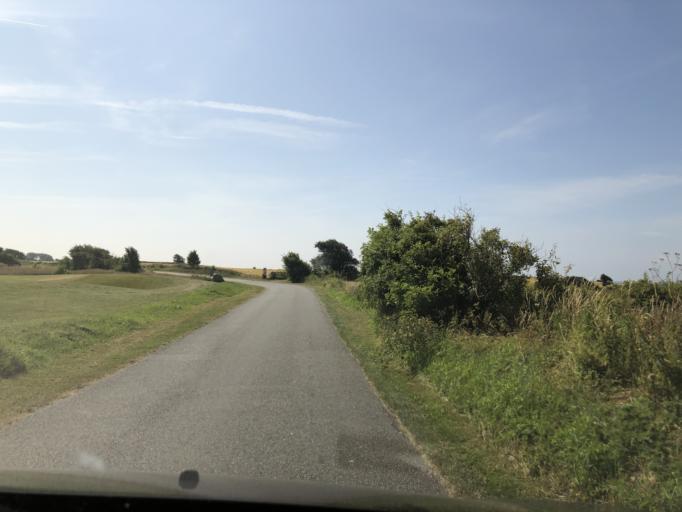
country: DK
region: South Denmark
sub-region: Faaborg-Midtfyn Kommune
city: Faaborg
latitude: 54.9632
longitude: 10.2123
